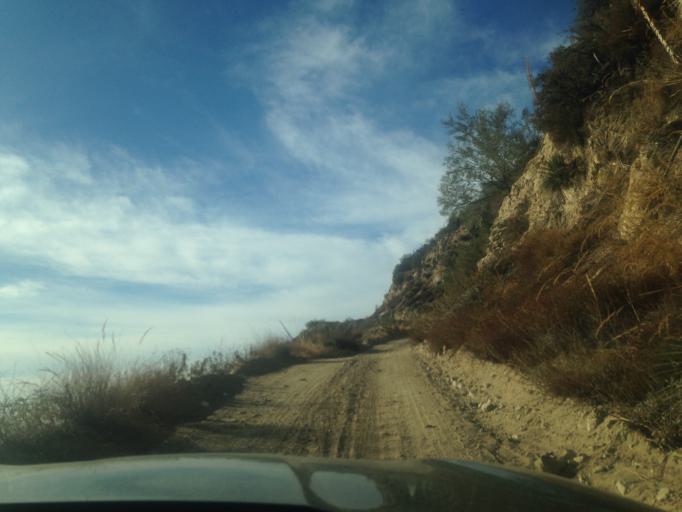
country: US
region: California
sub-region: San Bernardino County
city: Yucaipa
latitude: 34.1173
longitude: -117.0359
